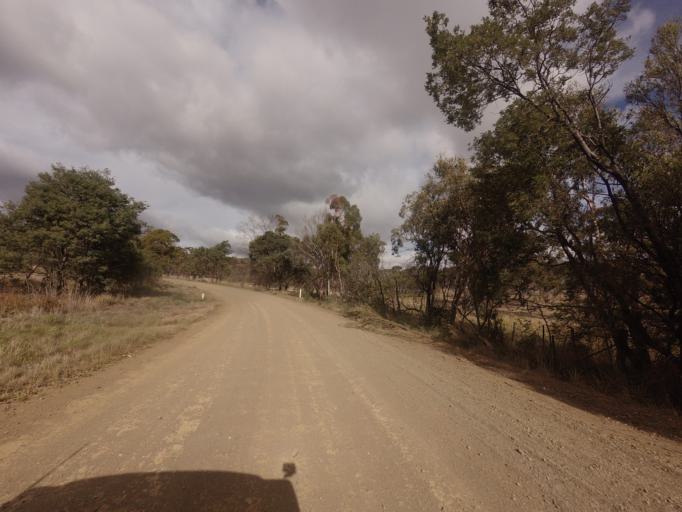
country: AU
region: Tasmania
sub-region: Brighton
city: Bridgewater
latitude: -42.4535
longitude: 147.2426
